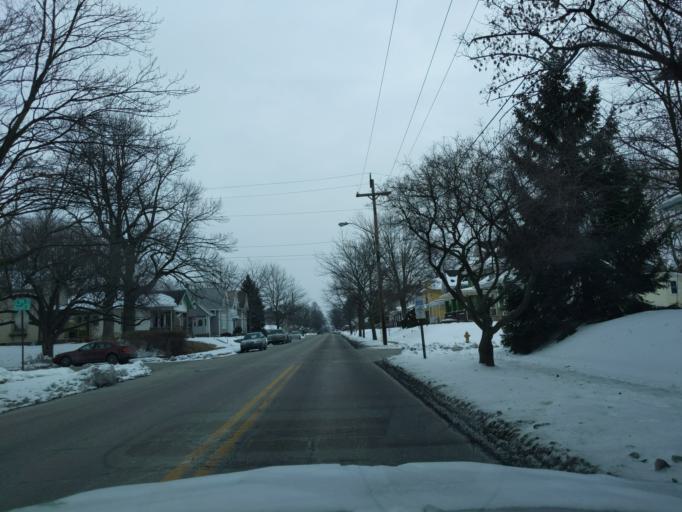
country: US
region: Indiana
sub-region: Tippecanoe County
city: Lafayette
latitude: 40.4100
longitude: -86.8846
